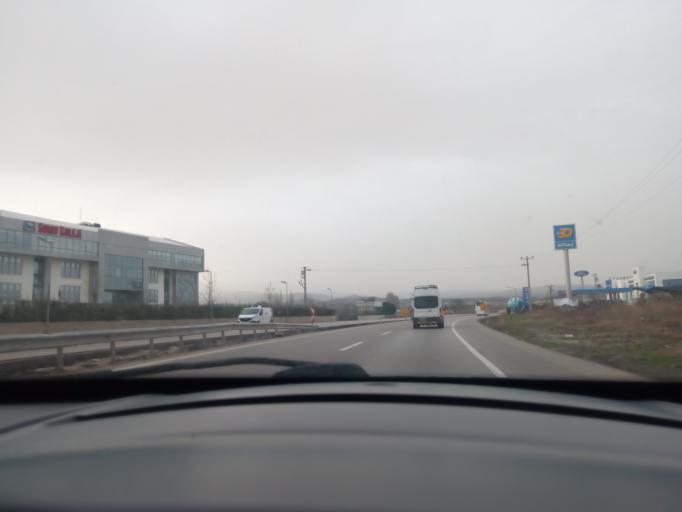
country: TR
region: Bursa
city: Tatkavakli
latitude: 40.0364
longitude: 28.3758
